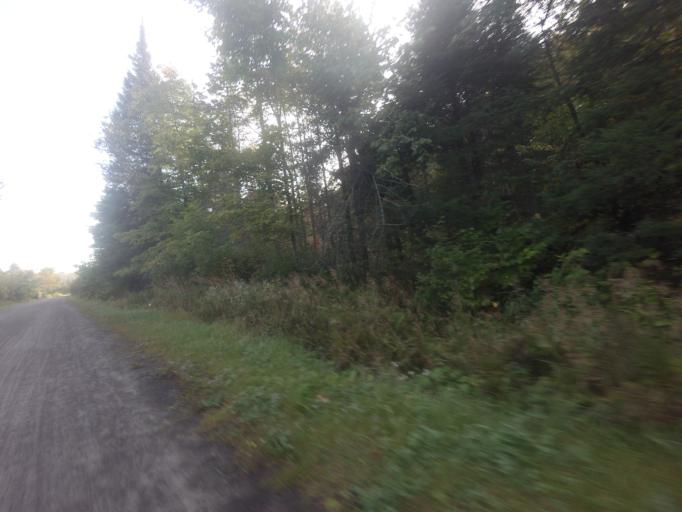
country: CA
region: Quebec
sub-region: Laurentides
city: Sainte-Adele
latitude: 45.9556
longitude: -74.1089
